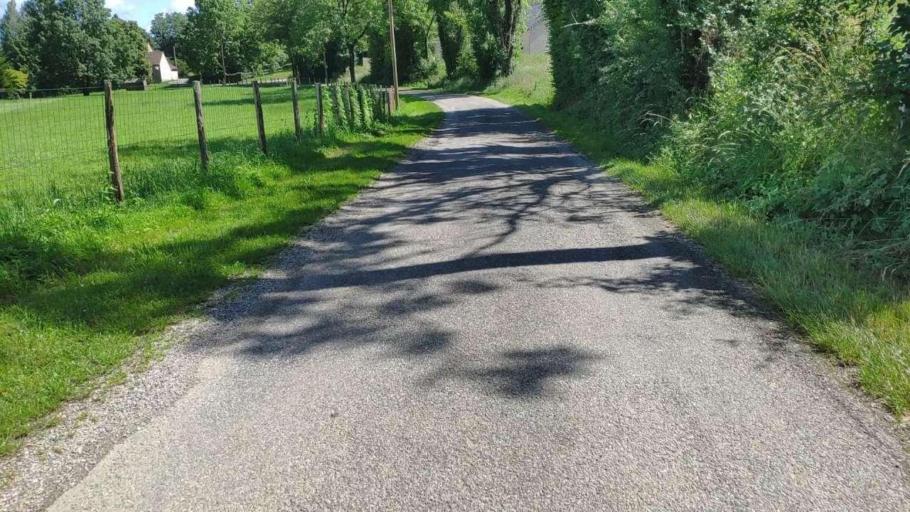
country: FR
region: Franche-Comte
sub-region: Departement du Jura
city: Bletterans
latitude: 46.8260
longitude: 5.5571
